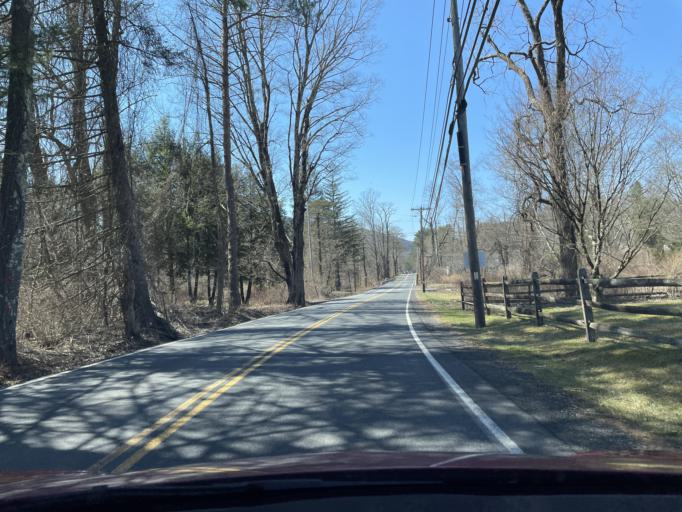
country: US
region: New York
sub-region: Ulster County
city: Shokan
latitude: 42.0282
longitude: -74.1865
